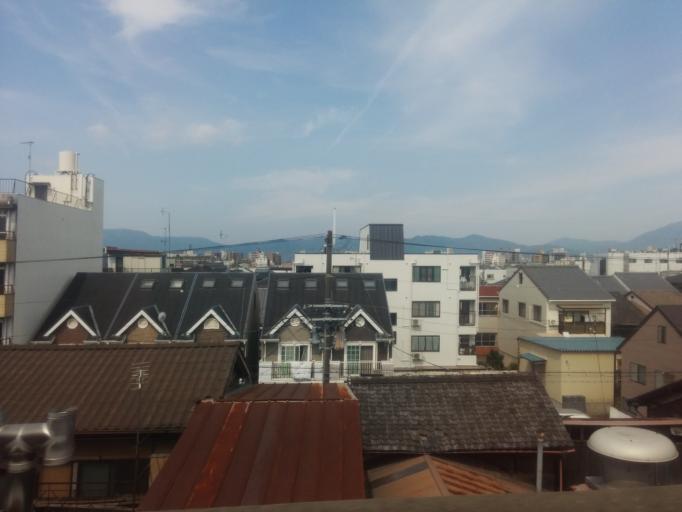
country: JP
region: Kyoto
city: Kyoto
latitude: 34.9996
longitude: 135.7418
